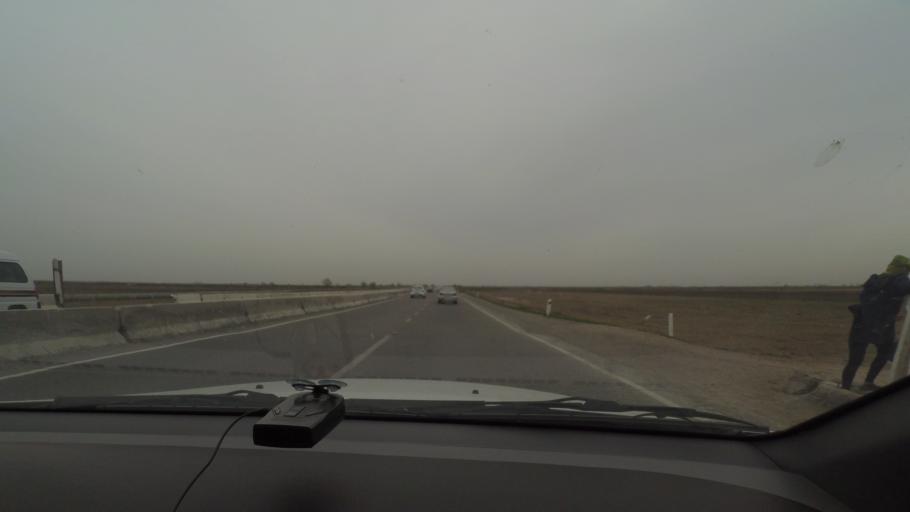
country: KZ
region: Ongtustik Qazaqstan
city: Myrzakent
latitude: 40.5194
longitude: 68.4687
